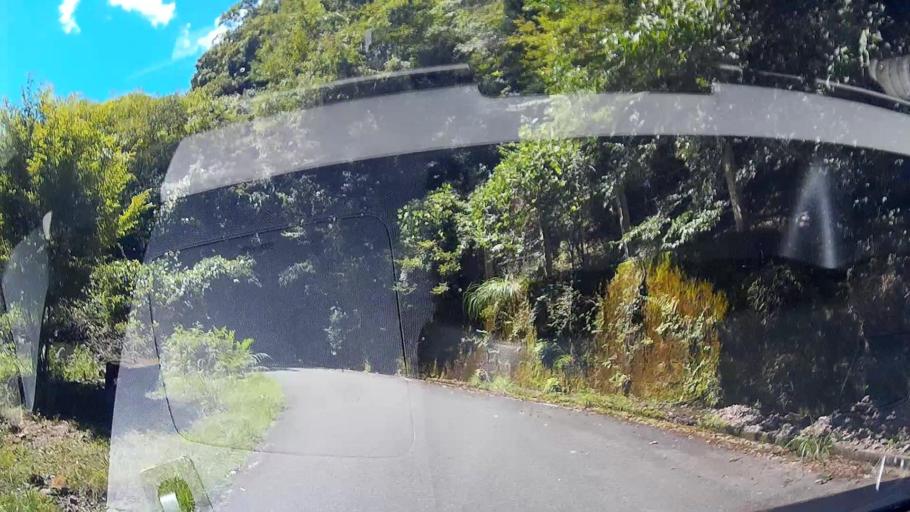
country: JP
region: Shizuoka
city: Shizuoka-shi
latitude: 35.1854
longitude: 138.2690
